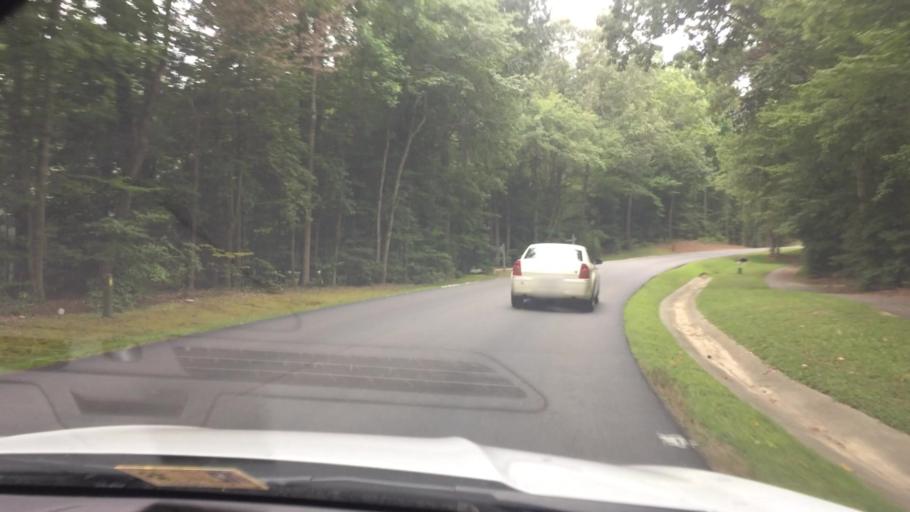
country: US
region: Virginia
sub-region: James City County
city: Williamsburg
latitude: 37.2969
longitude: -76.7786
